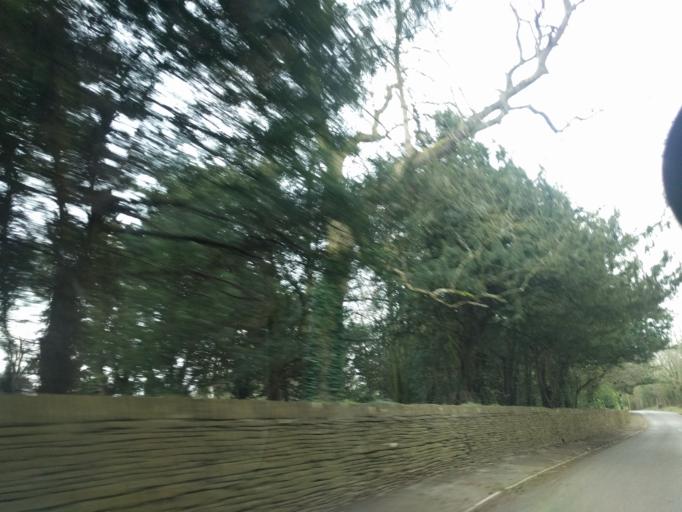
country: GB
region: England
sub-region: Wiltshire
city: Luckington
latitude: 51.5165
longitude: -2.2045
